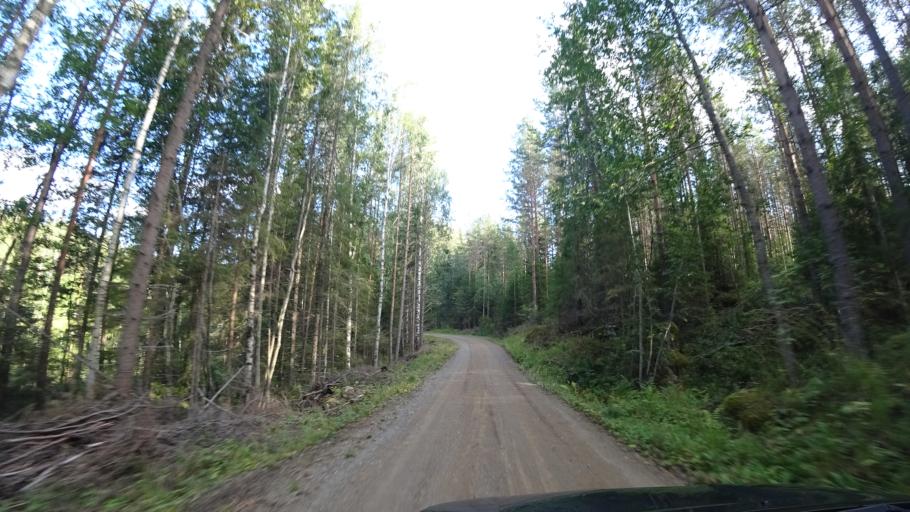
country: FI
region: Paijanne Tavastia
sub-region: Lahti
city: Auttoinen
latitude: 61.2222
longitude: 25.1989
